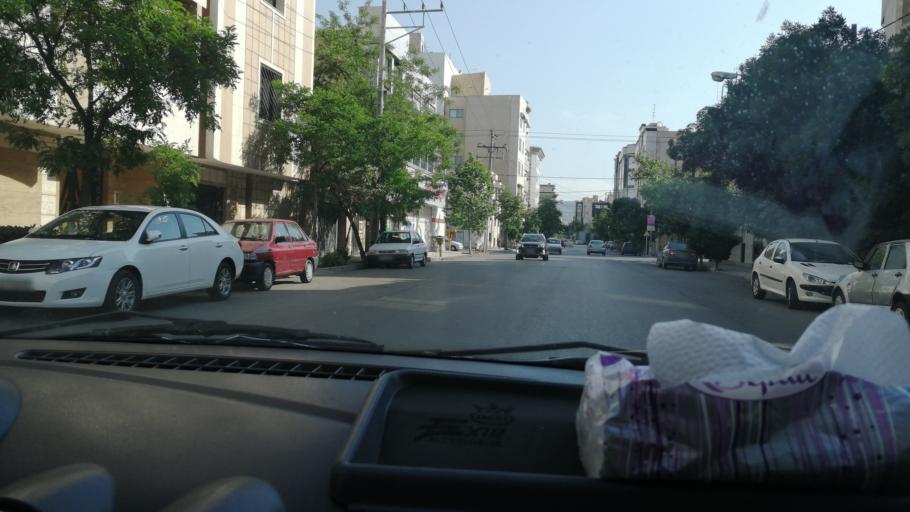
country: IR
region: Razavi Khorasan
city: Mashhad
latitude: 36.3108
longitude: 59.5612
